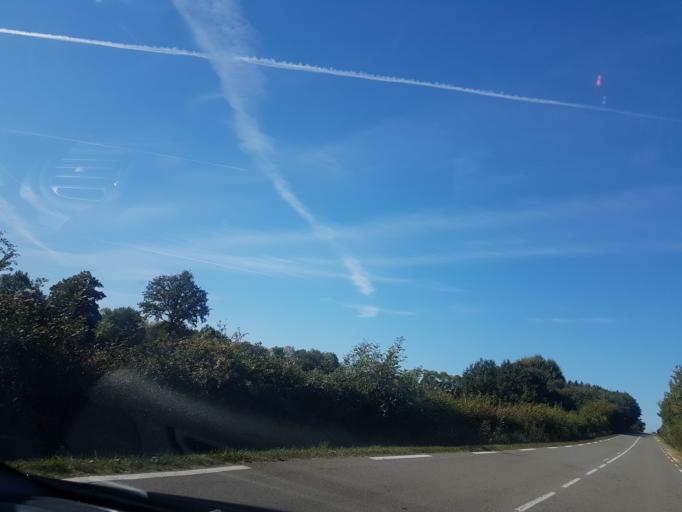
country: FR
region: Pays de la Loire
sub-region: Departement de la Loire-Atlantique
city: Casson
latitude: 47.4285
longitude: -1.5682
